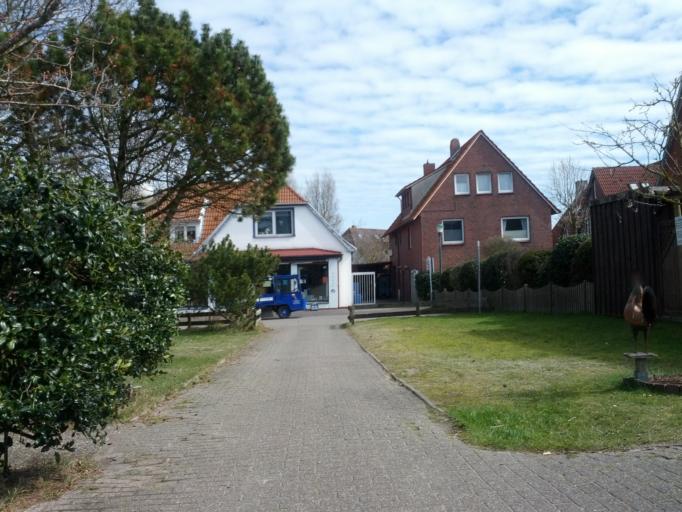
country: DE
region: Lower Saxony
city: Langeoog
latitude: 53.7460
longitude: 7.4824
